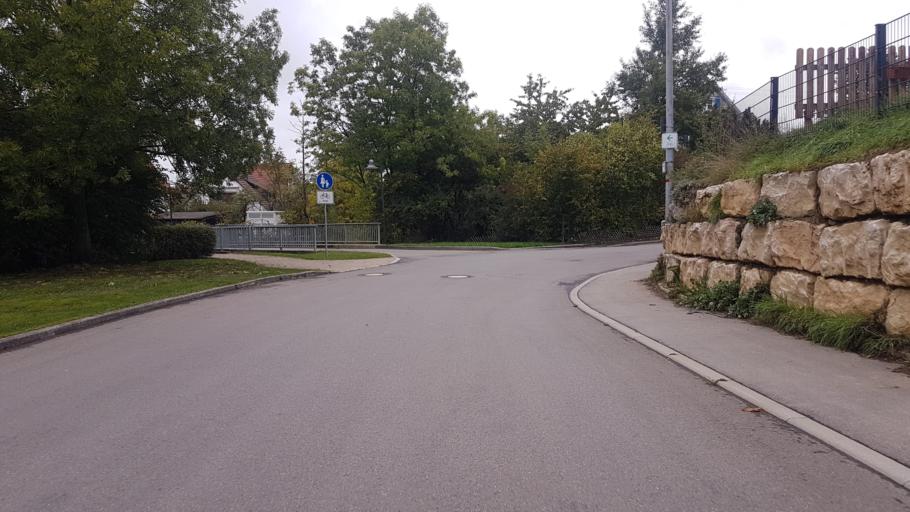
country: DE
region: Baden-Wuerttemberg
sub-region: Tuebingen Region
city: Dusslingen
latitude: 48.4471
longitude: 9.0552
